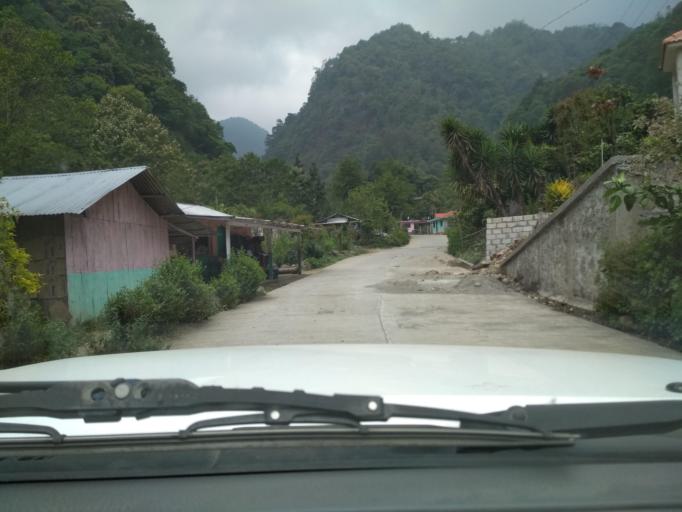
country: MX
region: Veracruz
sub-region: La Perla
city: Metlac Hernandez (Metlac Primero)
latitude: 18.9882
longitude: -97.1289
